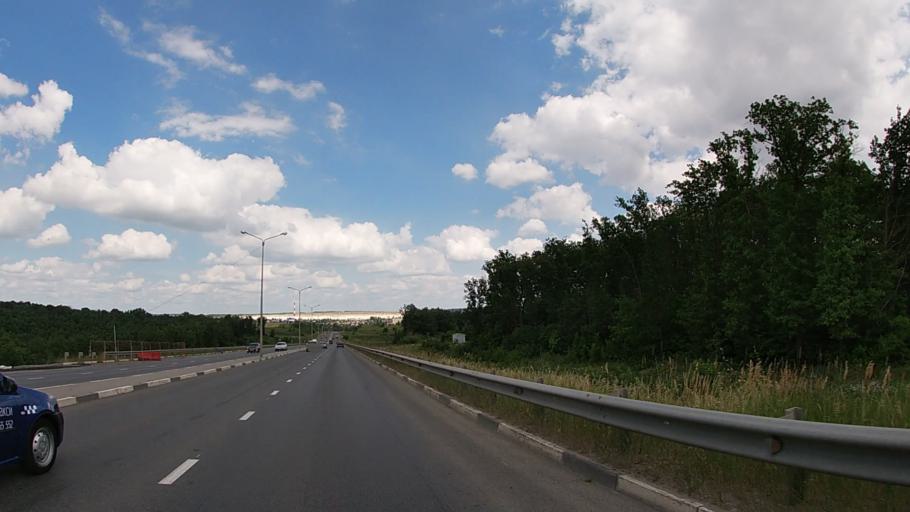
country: RU
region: Belgorod
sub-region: Belgorodskiy Rayon
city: Belgorod
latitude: 50.5971
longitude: 36.5305
